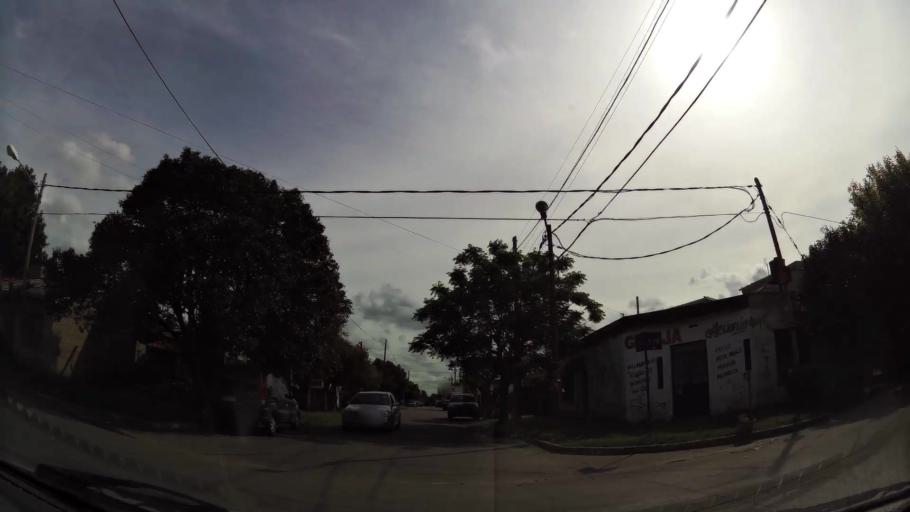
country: AR
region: Buenos Aires
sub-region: Partido de Quilmes
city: Quilmes
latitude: -34.7719
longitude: -58.2545
